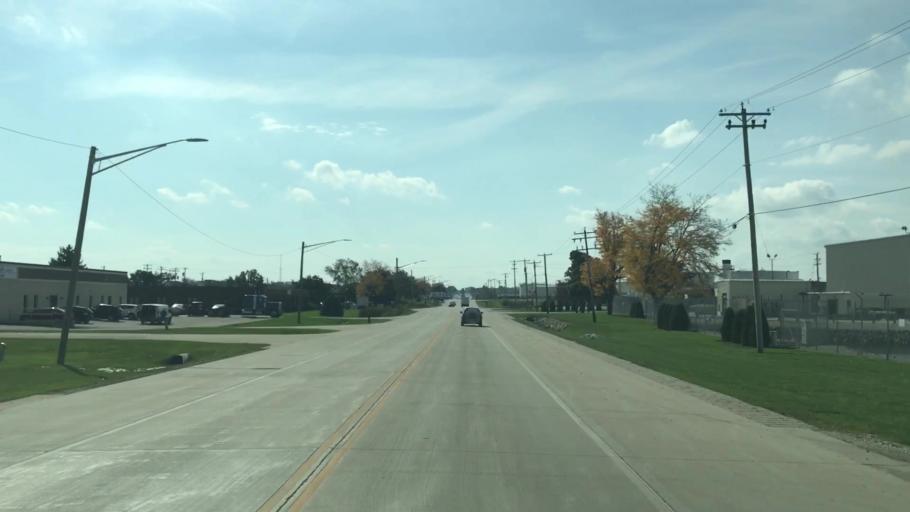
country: US
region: Wisconsin
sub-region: Waukesha County
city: Menomonee Falls
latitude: 43.1882
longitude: -88.0439
